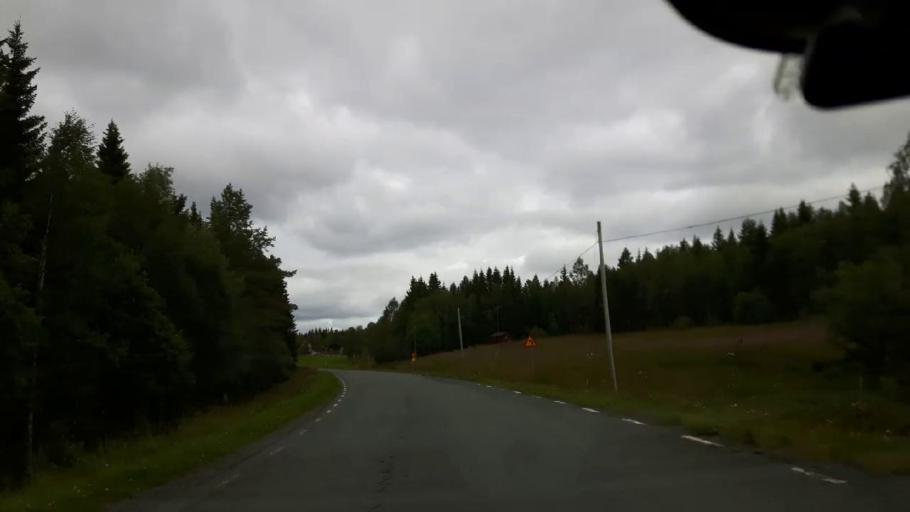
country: SE
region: Jaemtland
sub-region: Krokoms Kommun
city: Valla
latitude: 63.5331
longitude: 13.8725
